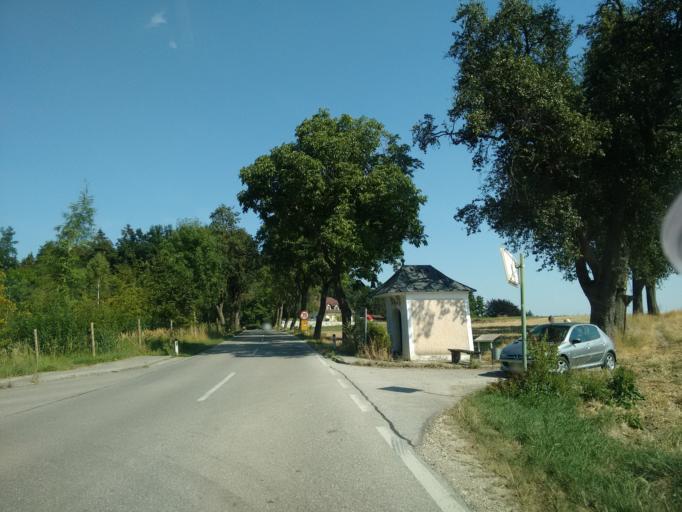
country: AT
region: Upper Austria
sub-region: Wels-Land
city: Gunskirchen
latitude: 48.1835
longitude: 13.9681
